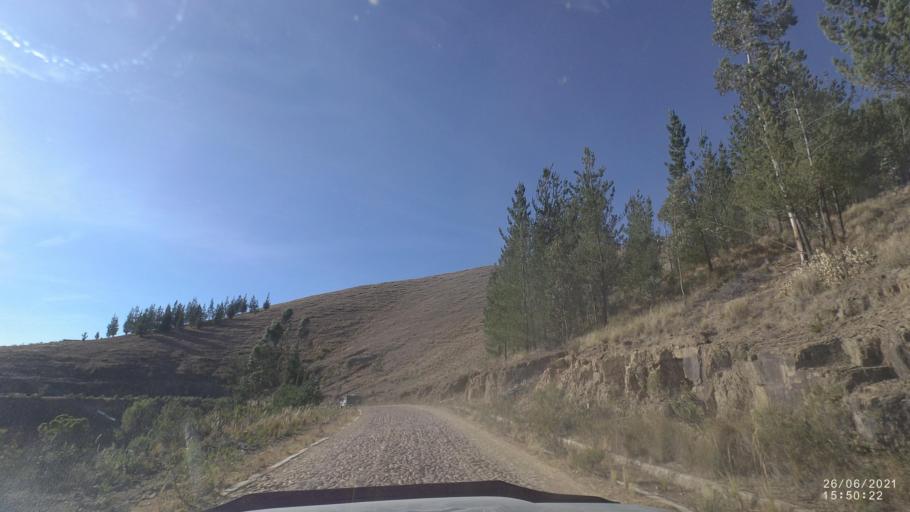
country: BO
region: Cochabamba
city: Arani
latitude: -17.8498
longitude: -65.7004
